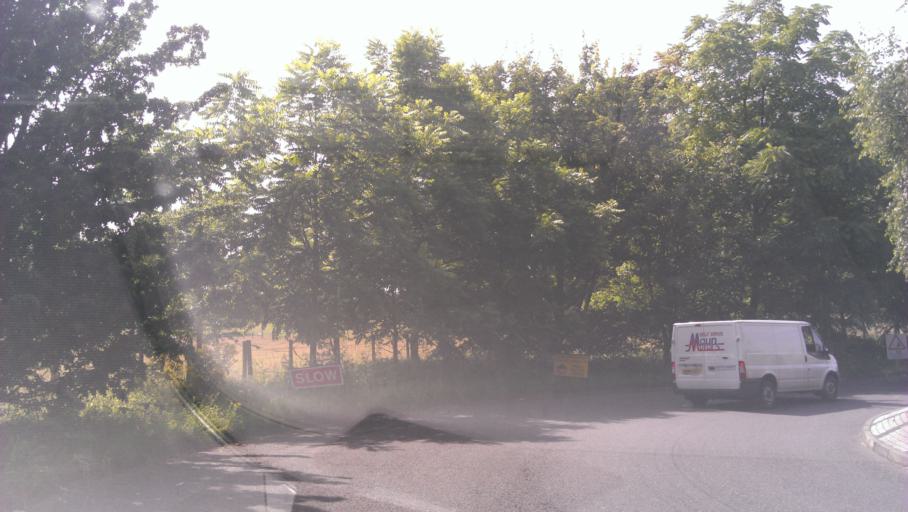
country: GB
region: England
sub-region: Kent
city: Faversham
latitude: 51.3137
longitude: 0.8647
